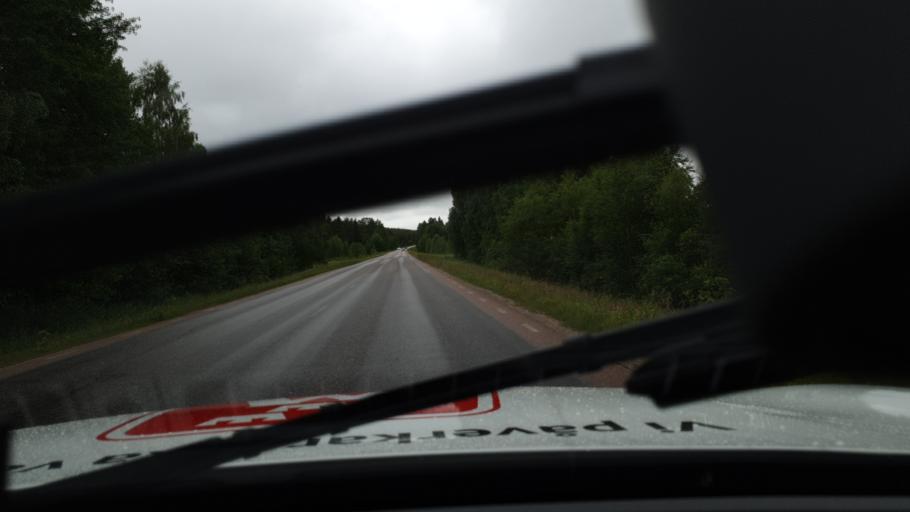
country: SE
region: Norrbotten
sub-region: Overtornea Kommun
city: OEvertornea
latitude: 66.4292
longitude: 23.6262
